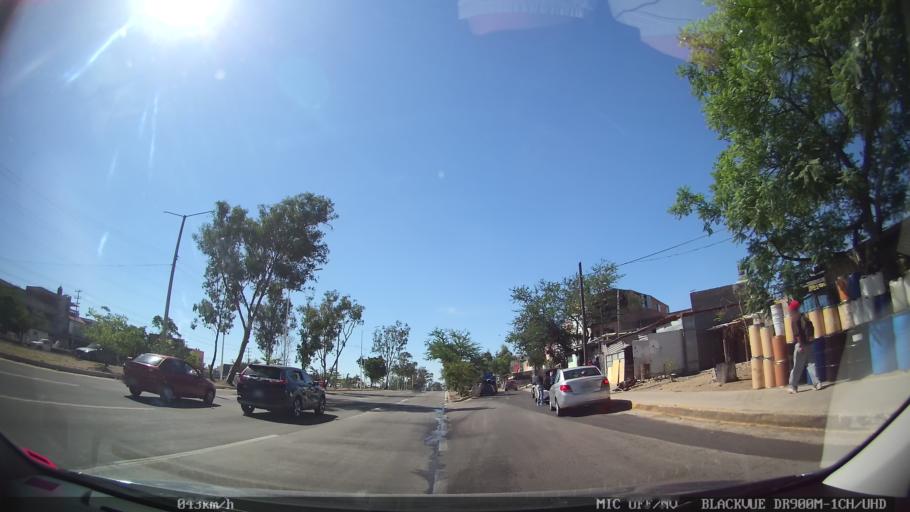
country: MX
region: Jalisco
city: Tlaquepaque
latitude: 20.7028
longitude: -103.2814
